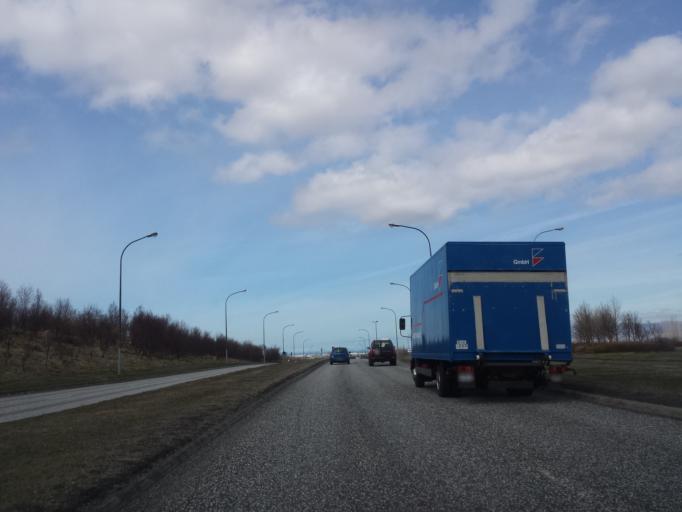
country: IS
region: Capital Region
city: Reykjavik
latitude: 64.0999
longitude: -21.8294
